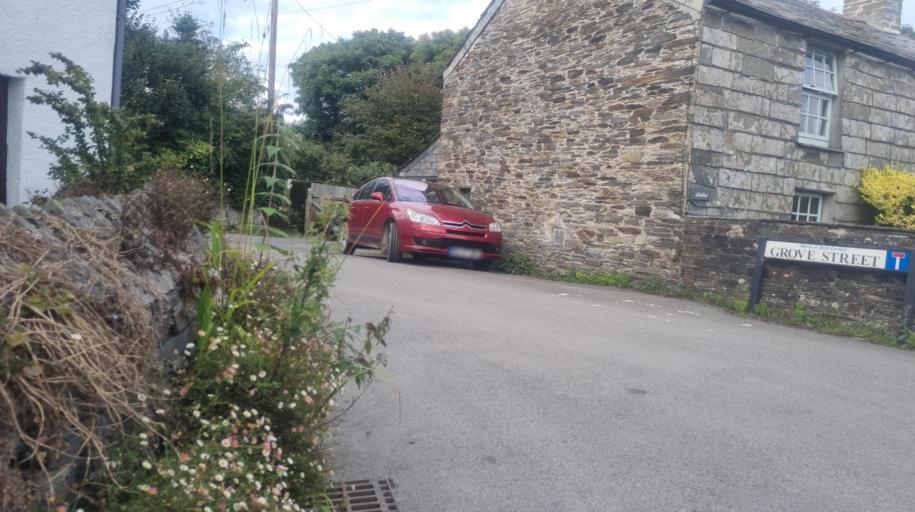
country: GB
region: England
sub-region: Cornwall
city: Camelford
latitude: 50.6207
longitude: -4.7257
